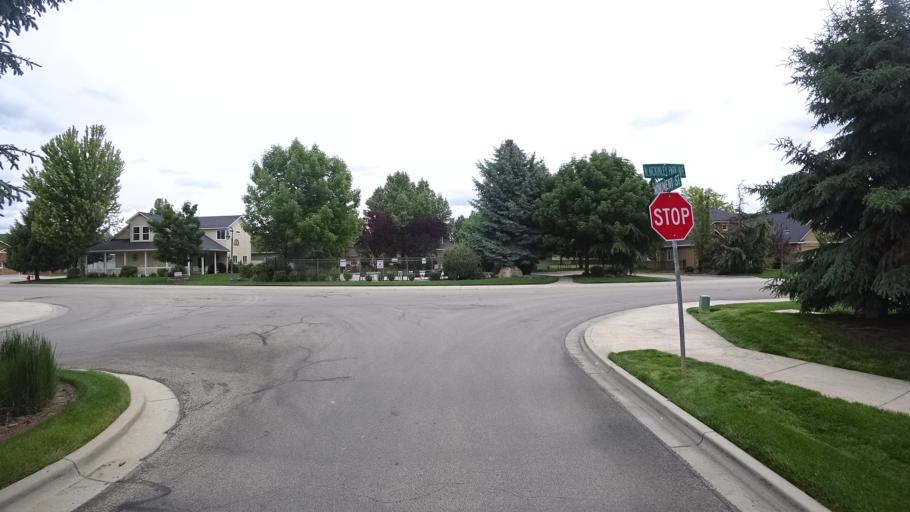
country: US
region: Idaho
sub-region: Ada County
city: Meridian
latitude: 43.6431
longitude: -116.4087
